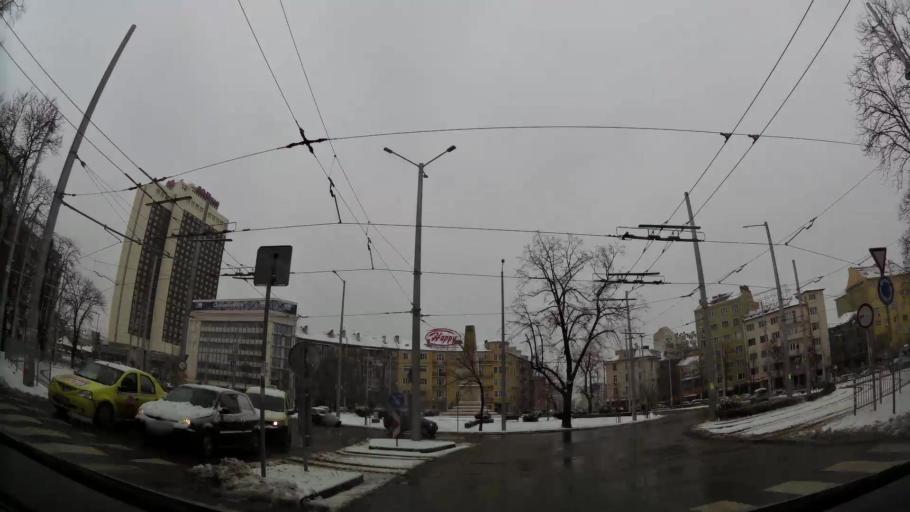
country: BG
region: Sofia-Capital
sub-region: Stolichna Obshtina
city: Sofia
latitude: 42.6919
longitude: 23.3109
